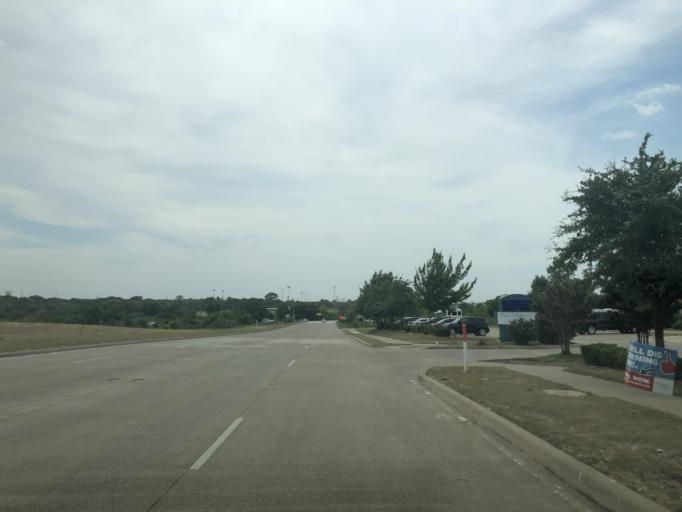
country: US
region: Texas
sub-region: Tarrant County
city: Blue Mound
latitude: 32.8944
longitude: -97.3459
